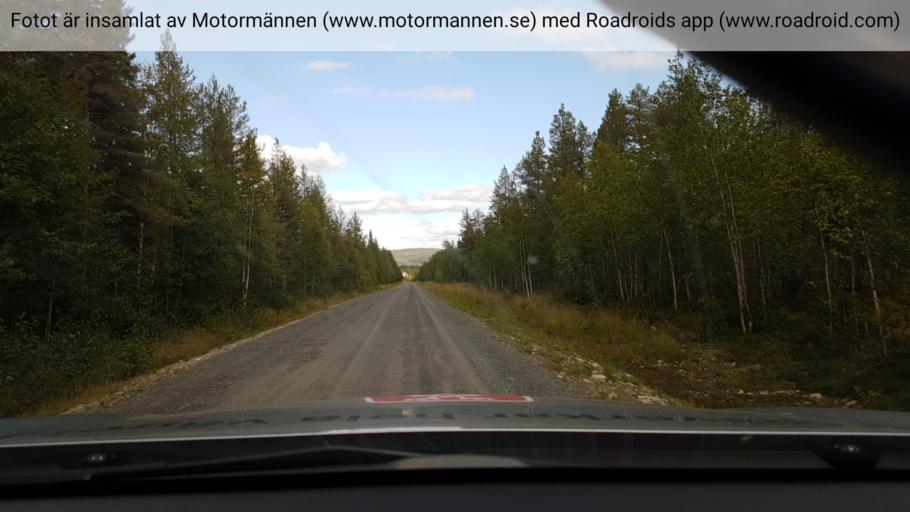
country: SE
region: Vaesterbotten
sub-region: Sorsele Kommun
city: Sorsele
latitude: 65.4595
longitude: 17.7434
